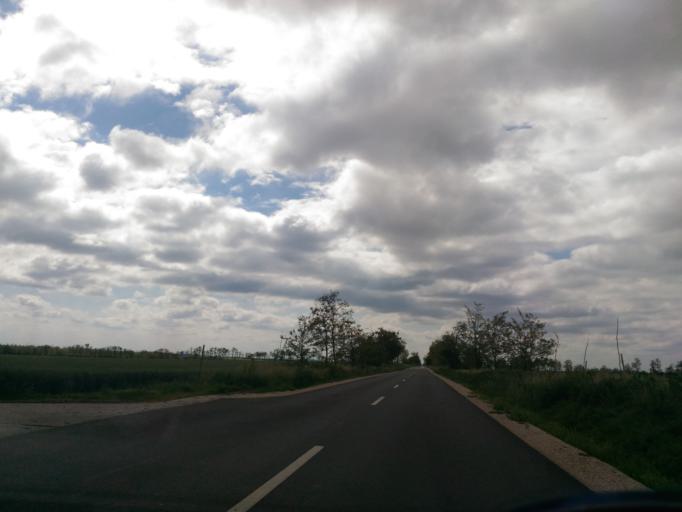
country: HU
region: Fejer
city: Kapolnasnyek
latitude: 47.1982
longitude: 18.6984
